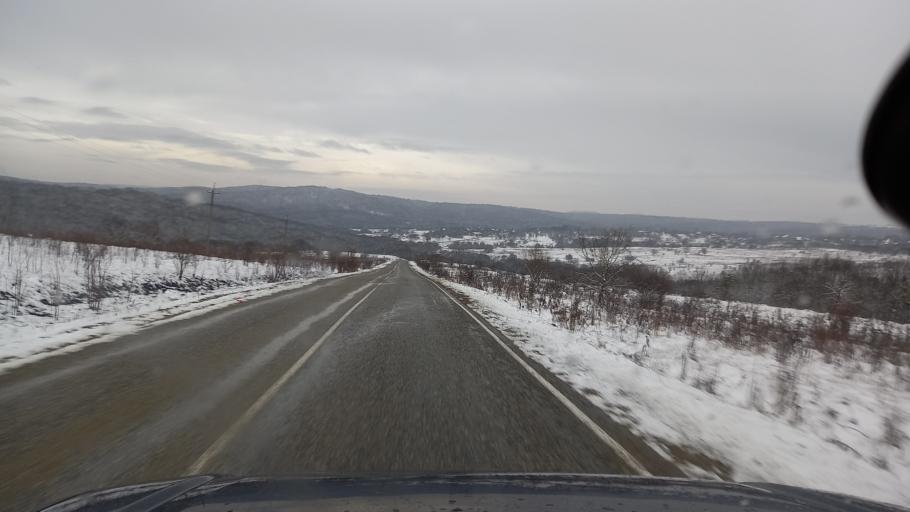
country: RU
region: Adygeya
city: Abadzekhskaya
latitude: 44.3590
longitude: 40.3882
